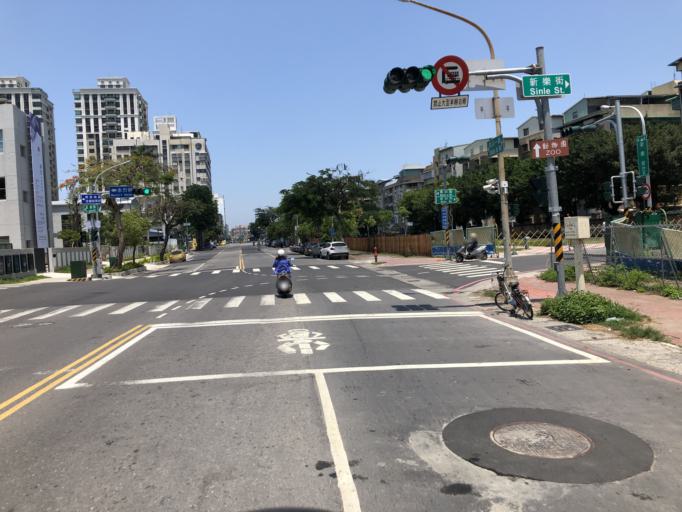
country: TW
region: Kaohsiung
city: Kaohsiung
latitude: 22.6270
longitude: 120.2787
